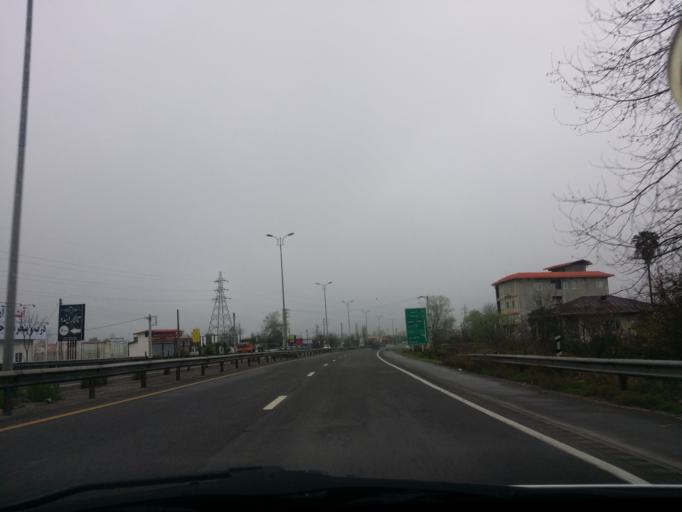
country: IR
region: Mazandaran
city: Tonekabon
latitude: 36.8112
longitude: 50.8578
